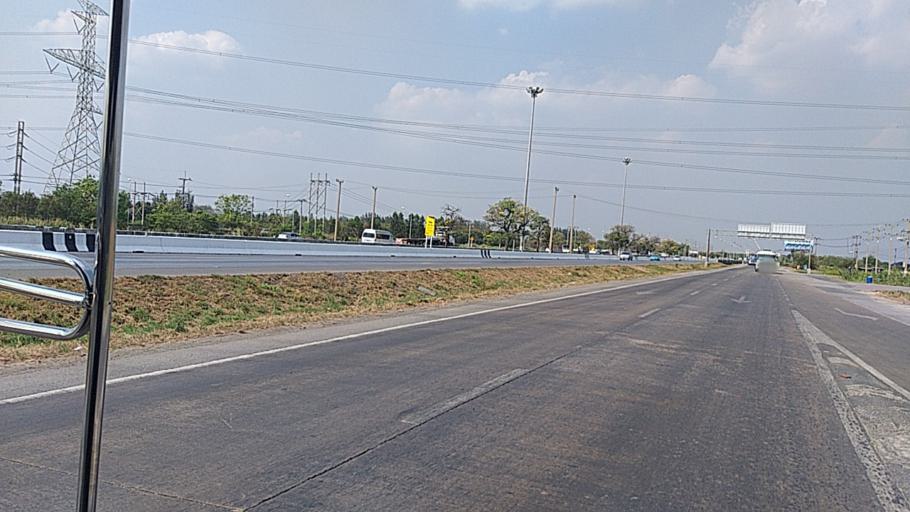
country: TH
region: Pathum Thani
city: Sam Khok
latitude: 14.0935
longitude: 100.5202
